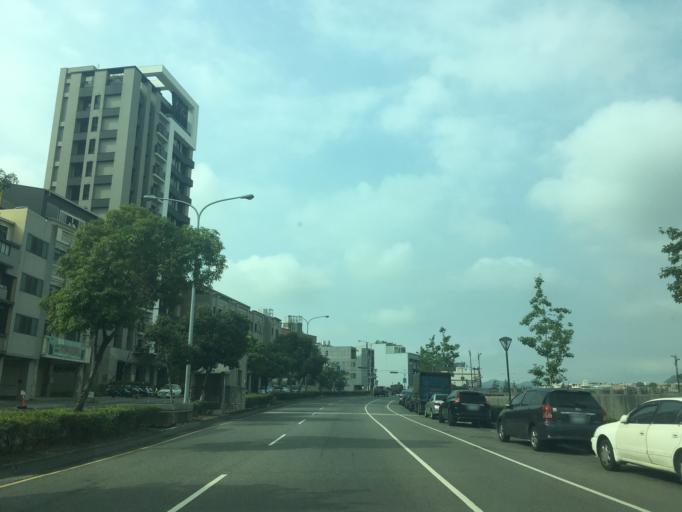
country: TW
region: Taiwan
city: Fengyuan
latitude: 24.2372
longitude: 120.7263
